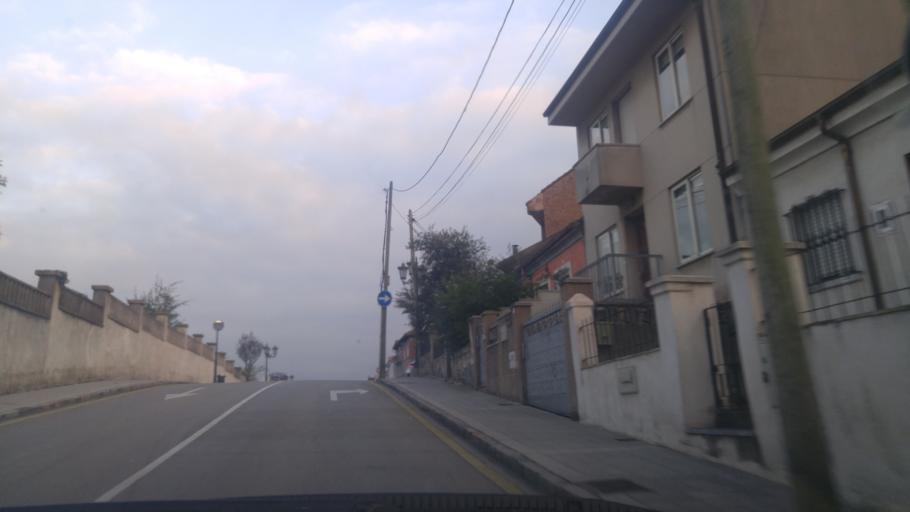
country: ES
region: Asturias
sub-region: Province of Asturias
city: Oviedo
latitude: 43.3728
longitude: -5.8579
